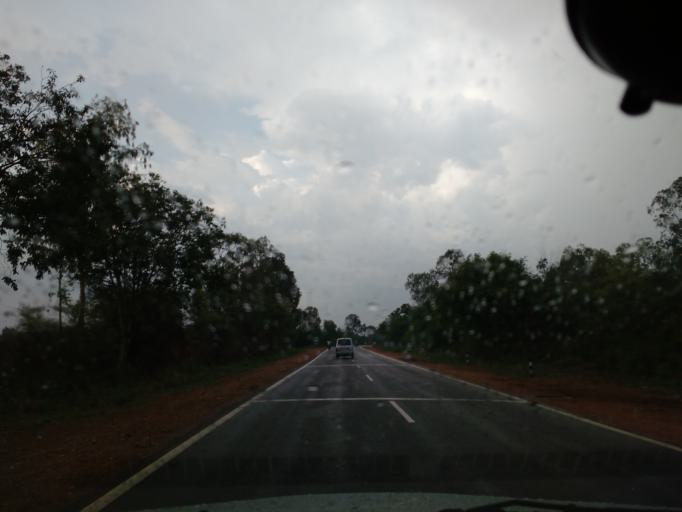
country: IN
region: Karnataka
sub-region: Tumkur
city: Tiptur
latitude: 13.2940
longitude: 76.5820
